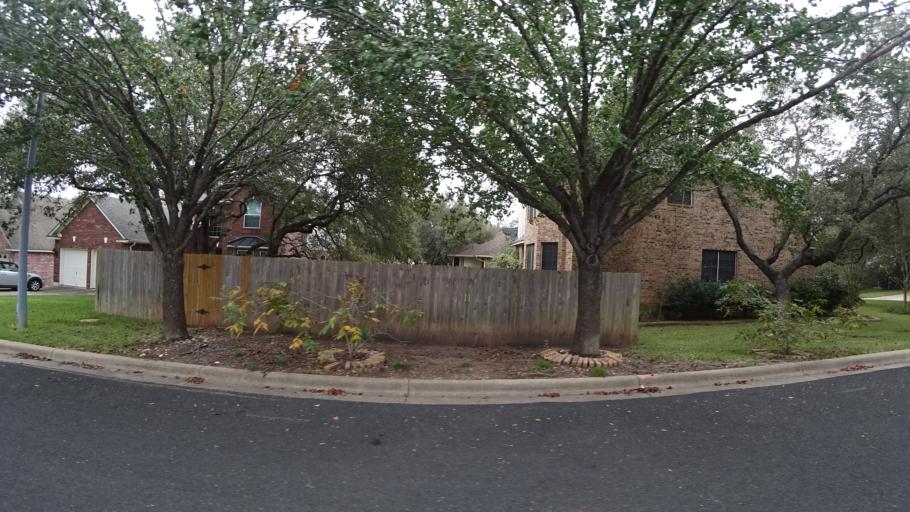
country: US
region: Texas
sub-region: Travis County
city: Shady Hollow
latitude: 30.2192
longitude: -97.8769
